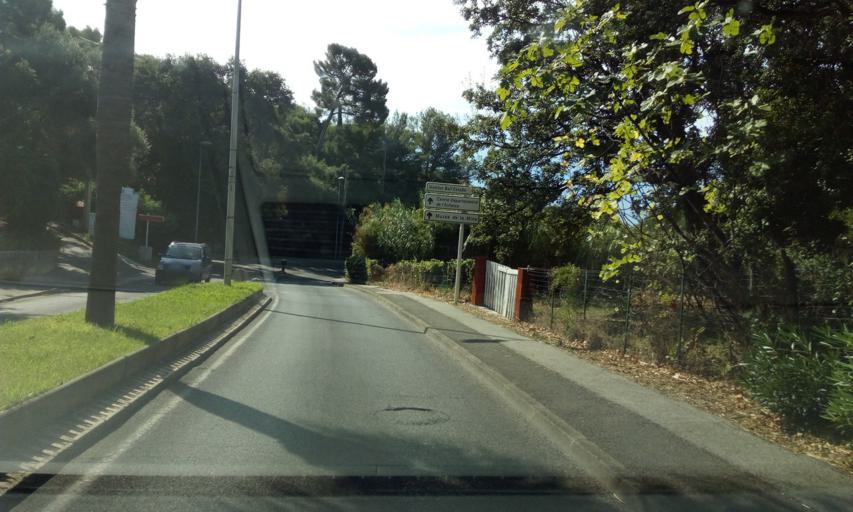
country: FR
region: Provence-Alpes-Cote d'Azur
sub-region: Departement du Var
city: Le Pradet
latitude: 43.1006
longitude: 6.0234
